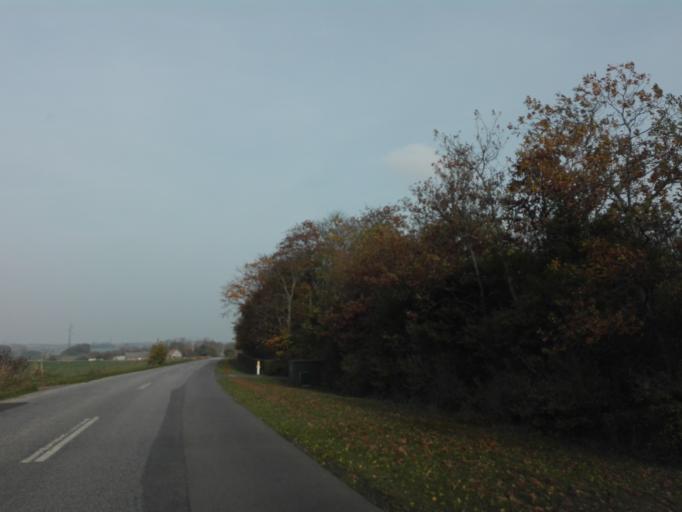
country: DK
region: Central Jutland
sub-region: Arhus Kommune
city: Solbjerg
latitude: 56.0566
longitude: 10.0878
